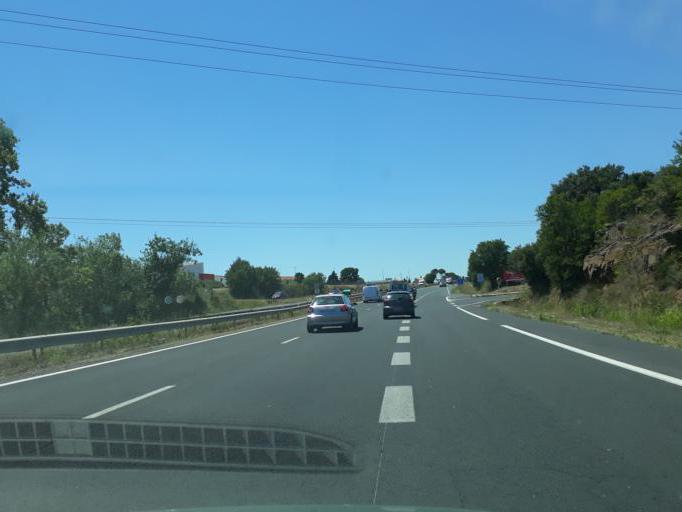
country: FR
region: Languedoc-Roussillon
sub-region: Departement de l'Herault
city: Le Cap d'Agde
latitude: 43.3078
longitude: 3.5075
